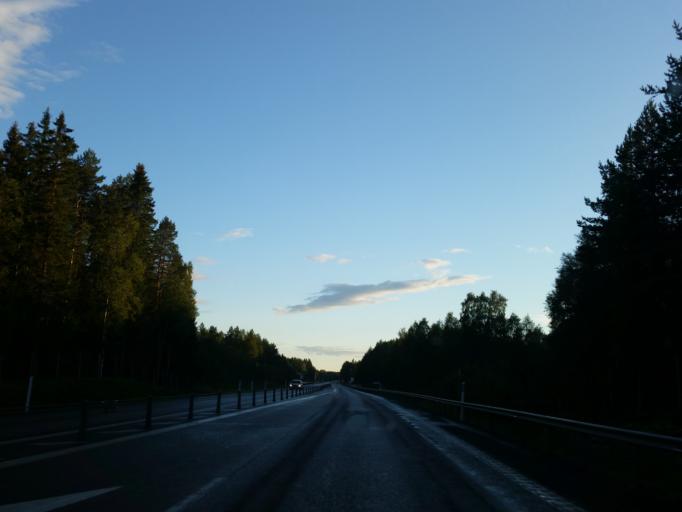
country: SE
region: Vaesterbotten
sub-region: Umea Kommun
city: Saevar
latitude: 63.9159
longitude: 20.5971
